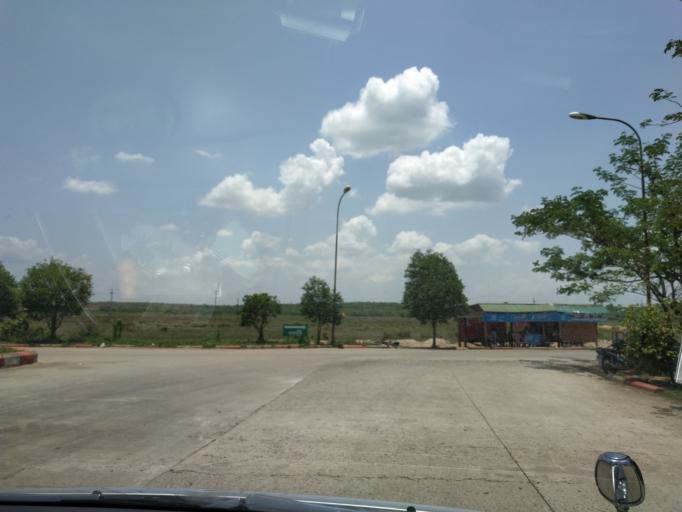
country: MM
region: Bago
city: Bago
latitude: 17.4704
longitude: 96.4534
